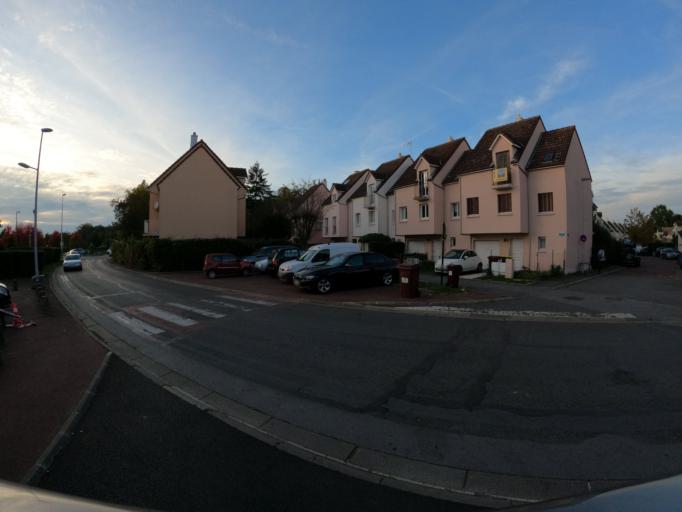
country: FR
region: Ile-de-France
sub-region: Departement de Seine-et-Marne
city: Emerainville
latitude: 48.8103
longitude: 2.6222
